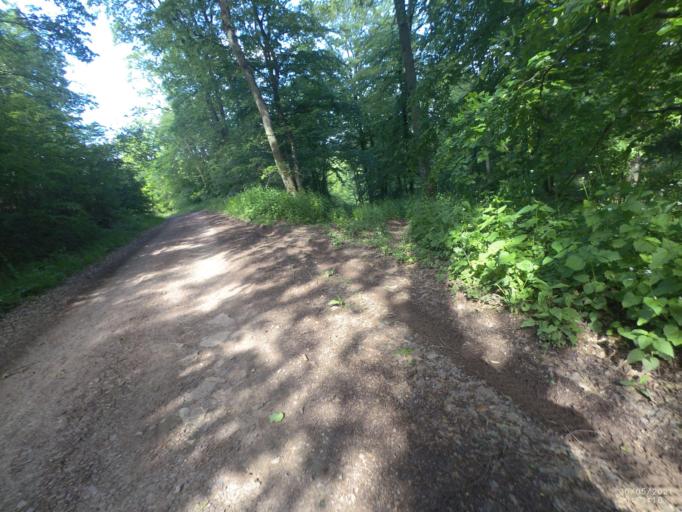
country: DE
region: Rheinland-Pfalz
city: Waldesch
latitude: 50.2733
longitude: 7.5655
